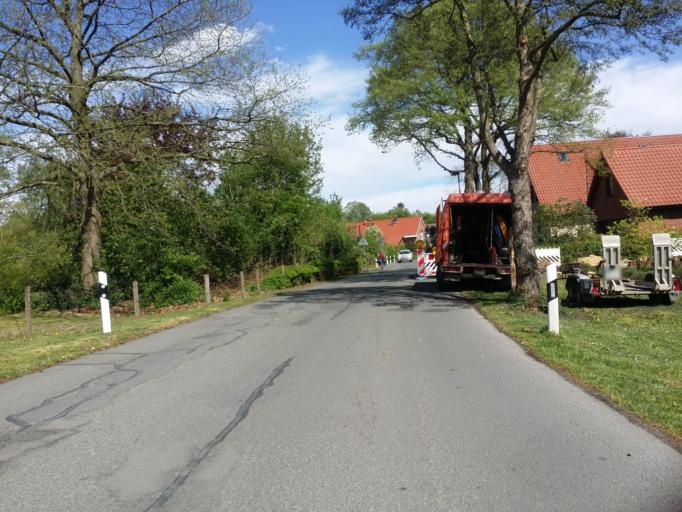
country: DE
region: Lower Saxony
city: Delmenhorst
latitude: 53.0719
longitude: 8.6560
